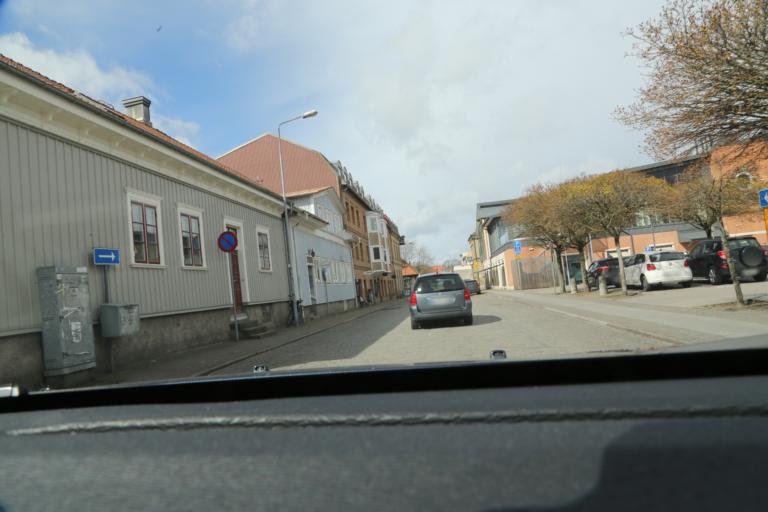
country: SE
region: Halland
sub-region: Varbergs Kommun
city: Varberg
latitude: 57.1042
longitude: 12.2511
